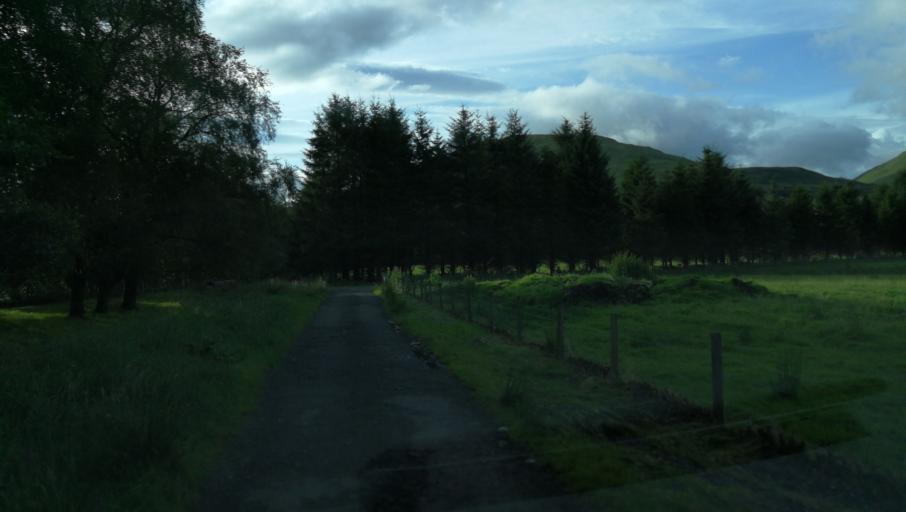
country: GB
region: Scotland
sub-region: Argyll and Bute
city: Garelochhead
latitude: 56.4192
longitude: -4.6696
